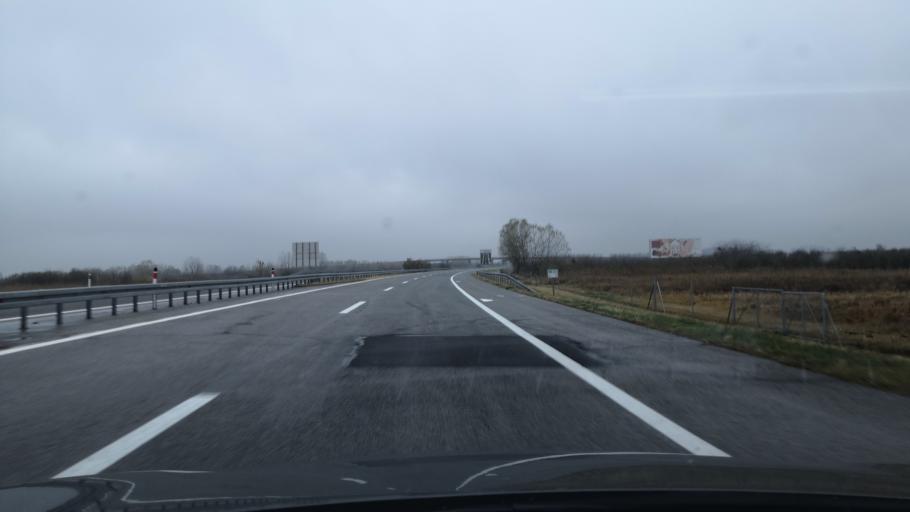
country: HU
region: Csongrad
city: Morahalom
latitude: 46.1484
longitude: 19.9309
